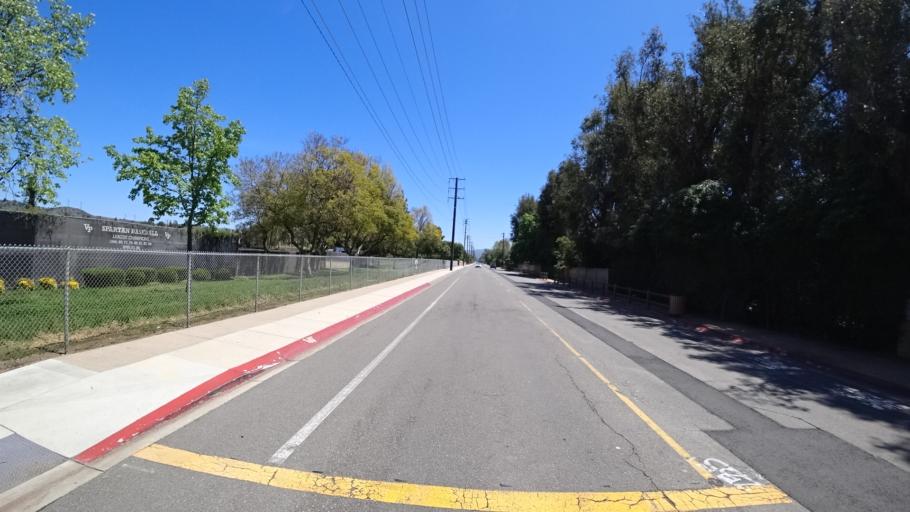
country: US
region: California
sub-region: Orange County
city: Villa Park
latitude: 33.8142
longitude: -117.8170
